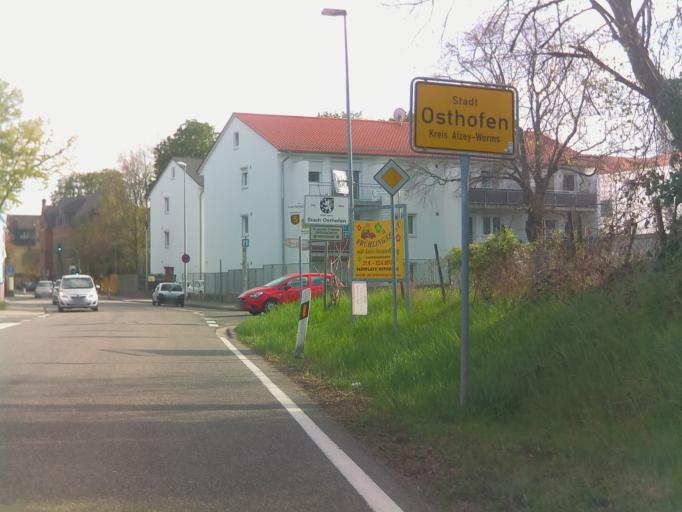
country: DE
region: Rheinland-Pfalz
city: Osthofen
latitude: 49.7074
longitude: 8.3241
